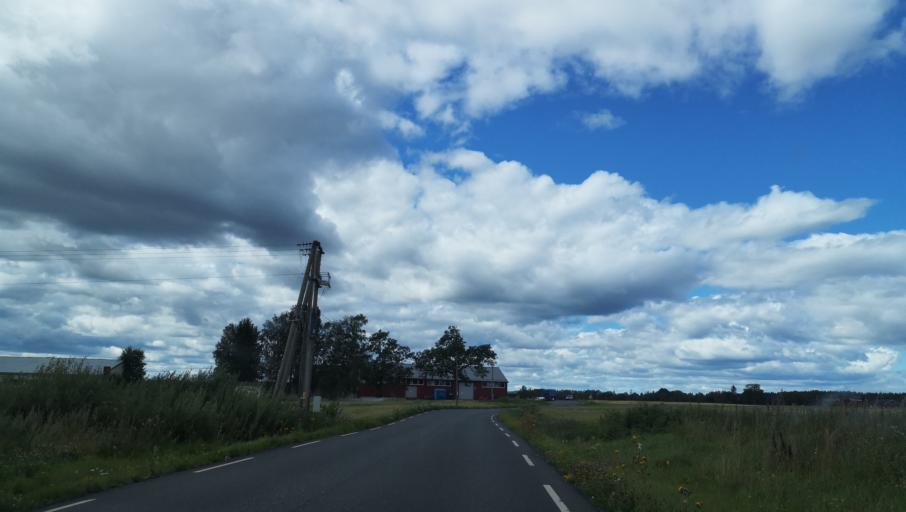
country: NO
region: Akershus
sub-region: Ski
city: Ski
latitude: 59.7083
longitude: 10.8875
